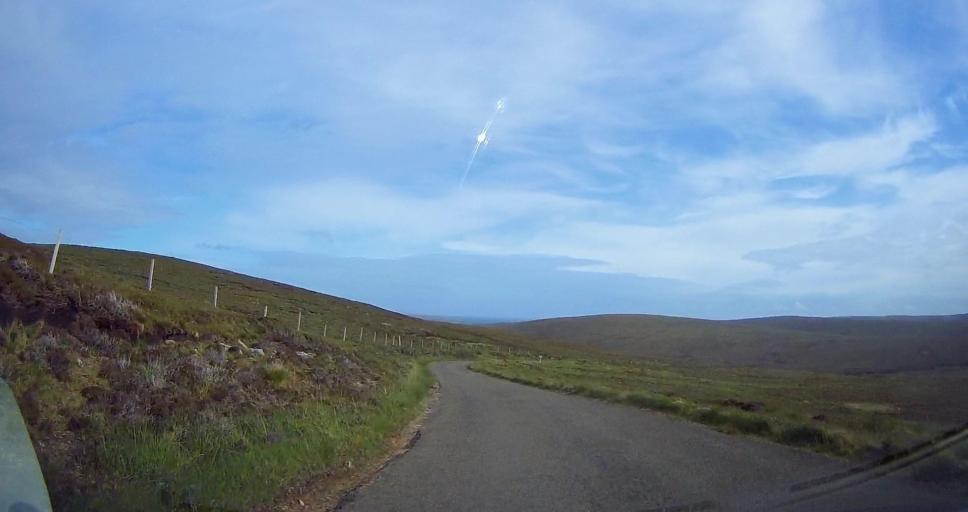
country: GB
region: Scotland
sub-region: Orkney Islands
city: Stromness
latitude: 58.8792
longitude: -3.2487
